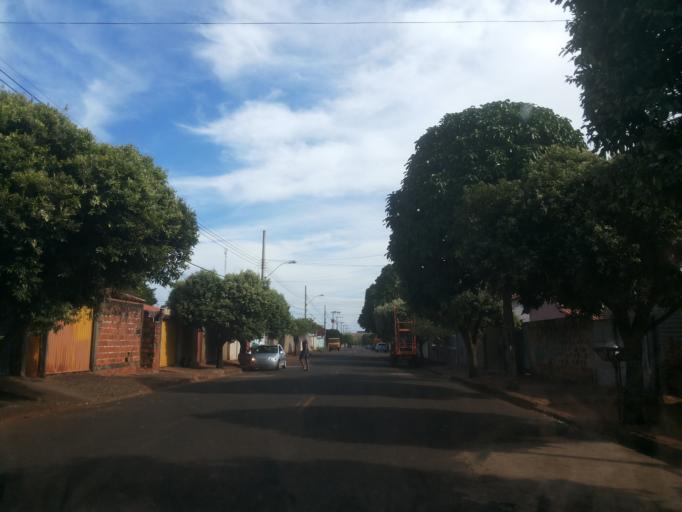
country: BR
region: Minas Gerais
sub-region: Centralina
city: Centralina
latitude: -18.7191
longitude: -49.2007
